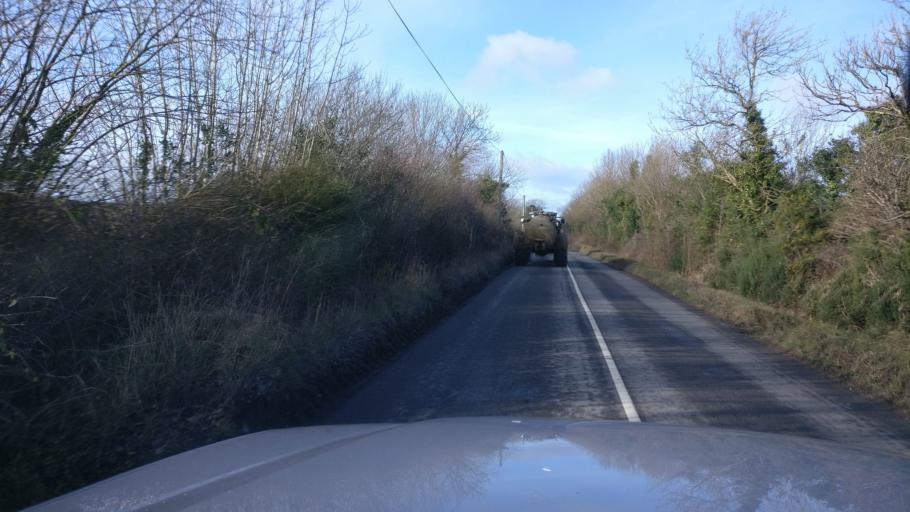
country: IE
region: Leinster
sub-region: Kilkenny
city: Castlecomer
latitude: 52.8937
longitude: -7.1687
